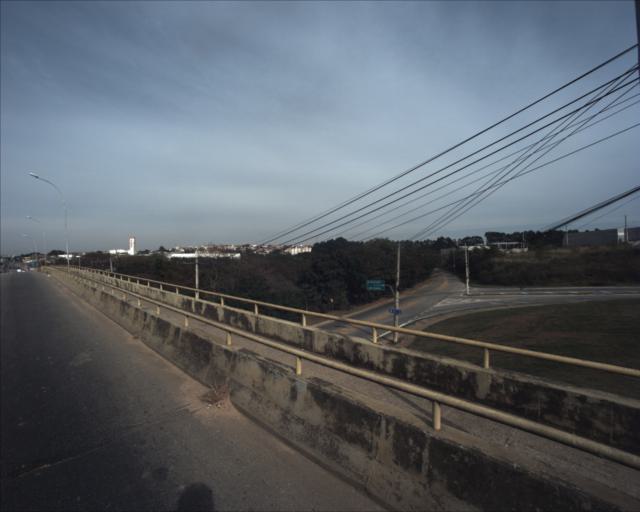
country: BR
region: Sao Paulo
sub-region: Sorocaba
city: Sorocaba
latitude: -23.4682
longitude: -47.4532
